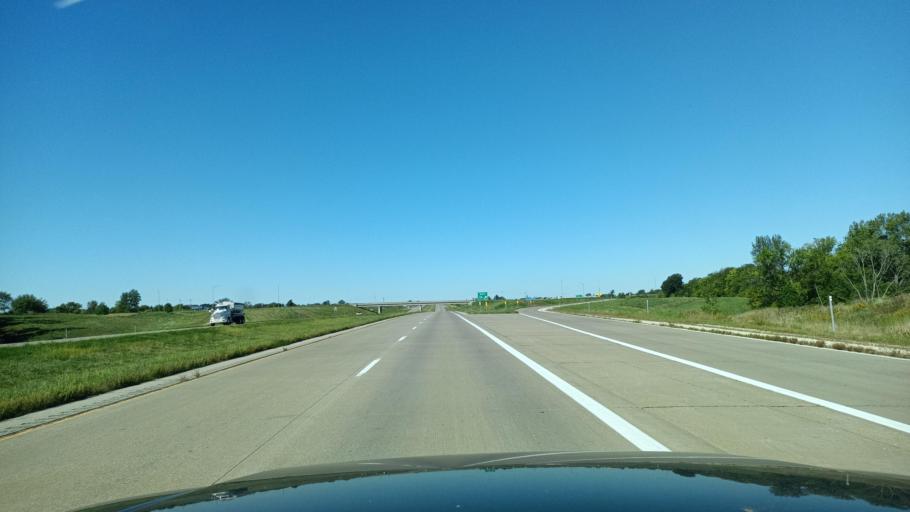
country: US
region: Iowa
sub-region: Lee County
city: Fort Madison
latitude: 40.6707
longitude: -91.3212
